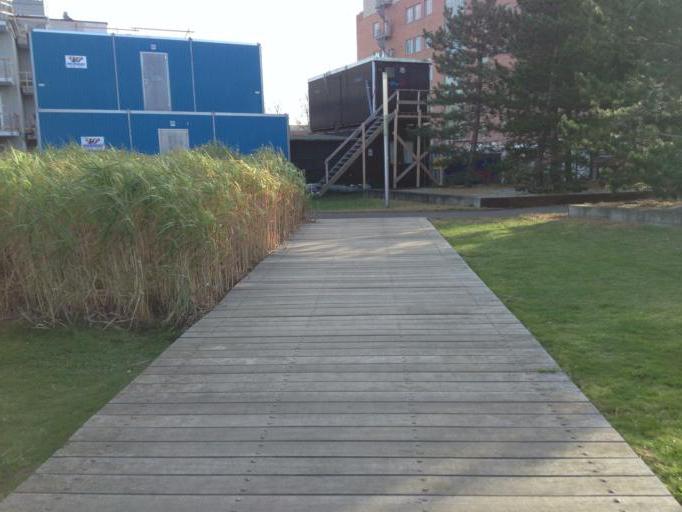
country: SE
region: Skane
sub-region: Malmo
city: Malmoe
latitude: 55.6104
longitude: 12.9762
